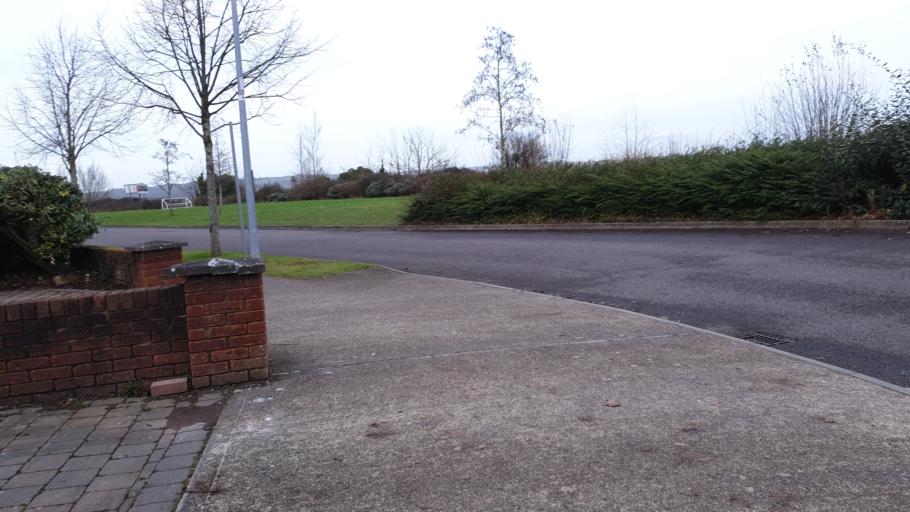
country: IE
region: Munster
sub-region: County Cork
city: Passage West
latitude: 51.8823
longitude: -8.3922
